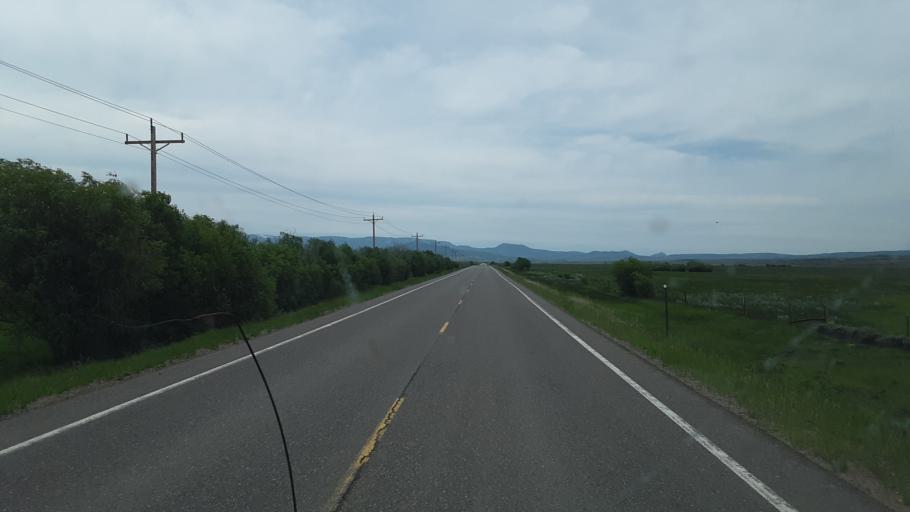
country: US
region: Colorado
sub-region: Jackson County
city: Walden
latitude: 40.5698
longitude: -106.4072
